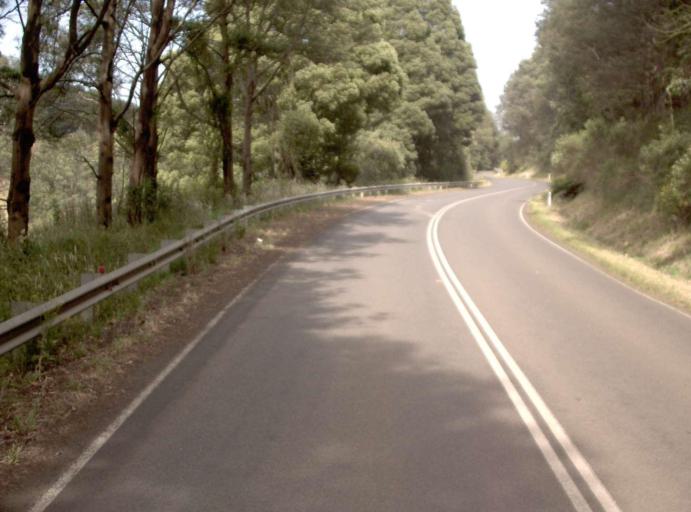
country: AU
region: Victoria
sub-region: Latrobe
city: Moe
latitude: -38.3308
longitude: 146.1880
